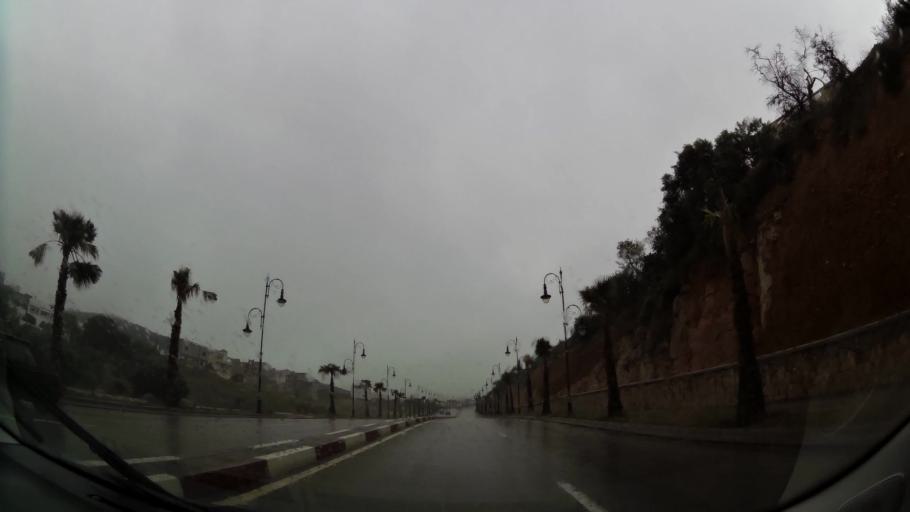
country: MA
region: Taza-Al Hoceima-Taounate
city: Tirhanimine
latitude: 35.2081
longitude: -3.9188
